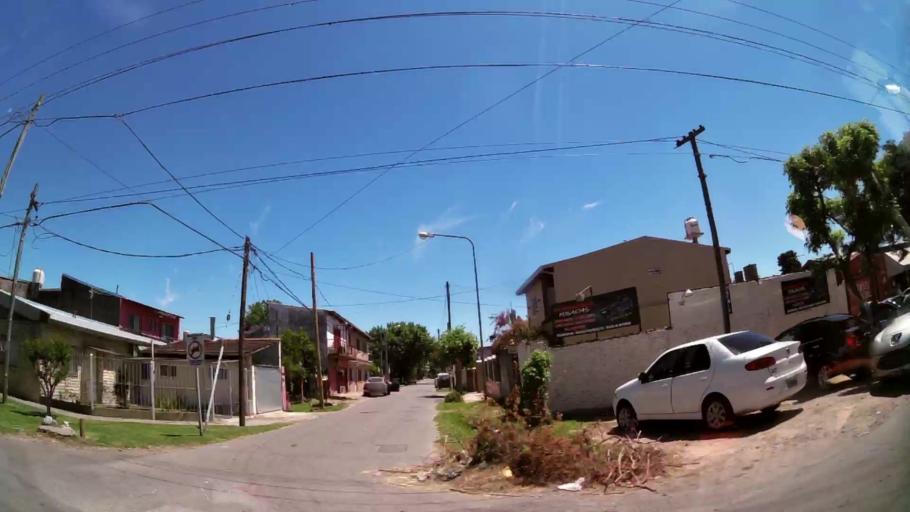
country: AR
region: Buenos Aires
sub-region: Partido de Tigre
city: Tigre
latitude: -34.4871
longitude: -58.6392
